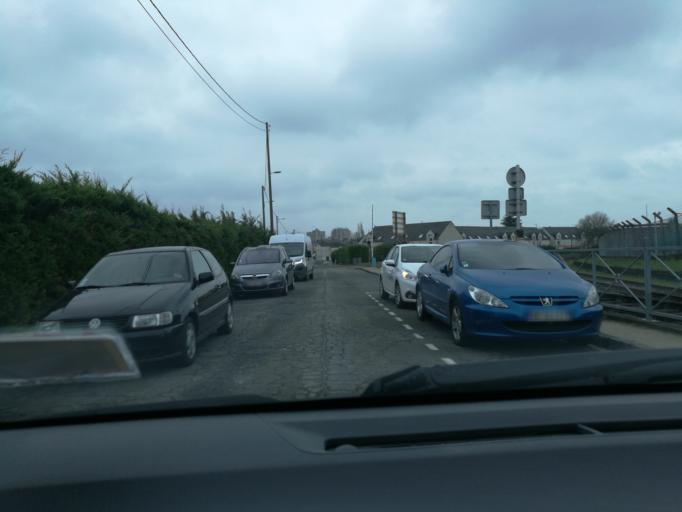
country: FR
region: Centre
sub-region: Departement du Loiret
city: Fleury-les-Aubrais
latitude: 47.9423
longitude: 1.9158
